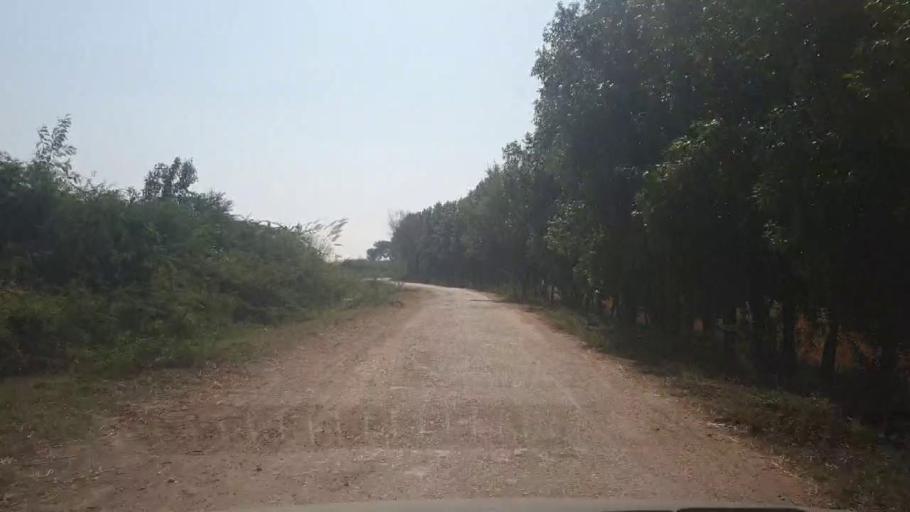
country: PK
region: Sindh
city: Badin
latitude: 24.6749
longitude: 68.8816
